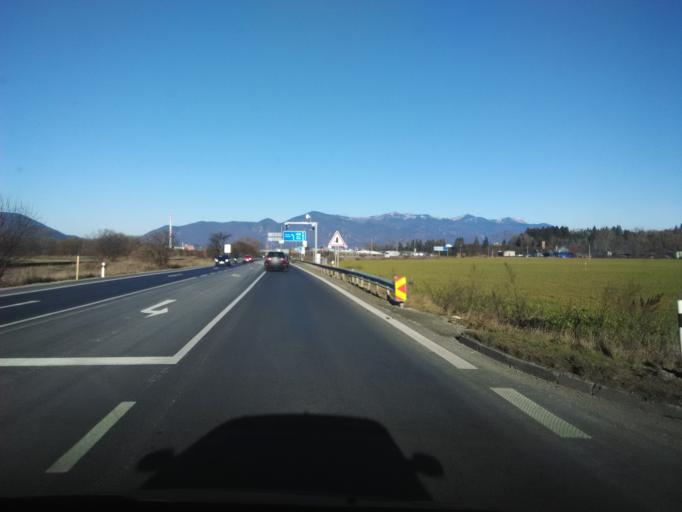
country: SK
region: Zilinsky
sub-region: Okres Martin
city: Martin
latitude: 49.0351
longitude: 18.9079
